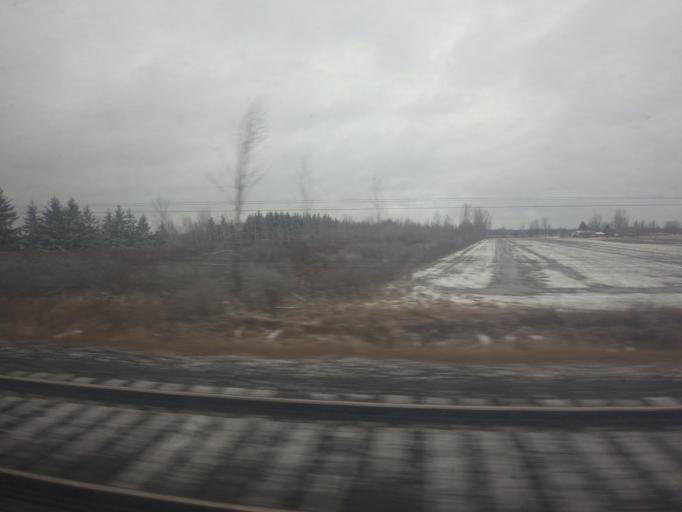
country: CA
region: Ontario
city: Gananoque
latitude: 44.3833
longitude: -76.0654
